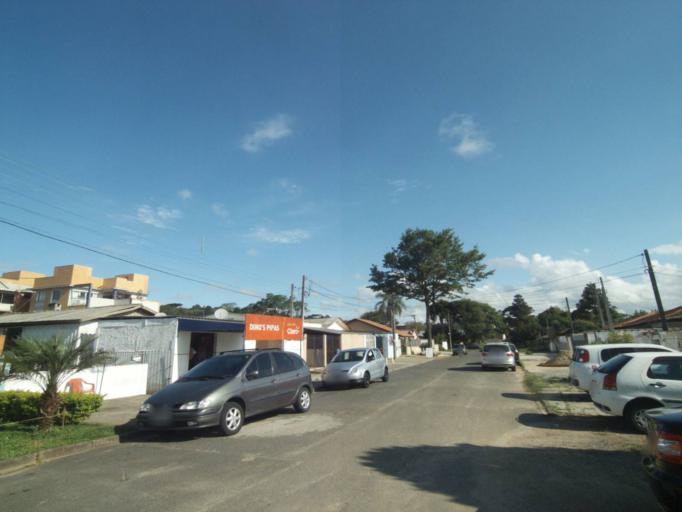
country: BR
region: Parana
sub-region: Curitiba
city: Curitiba
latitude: -25.3899
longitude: -49.3034
